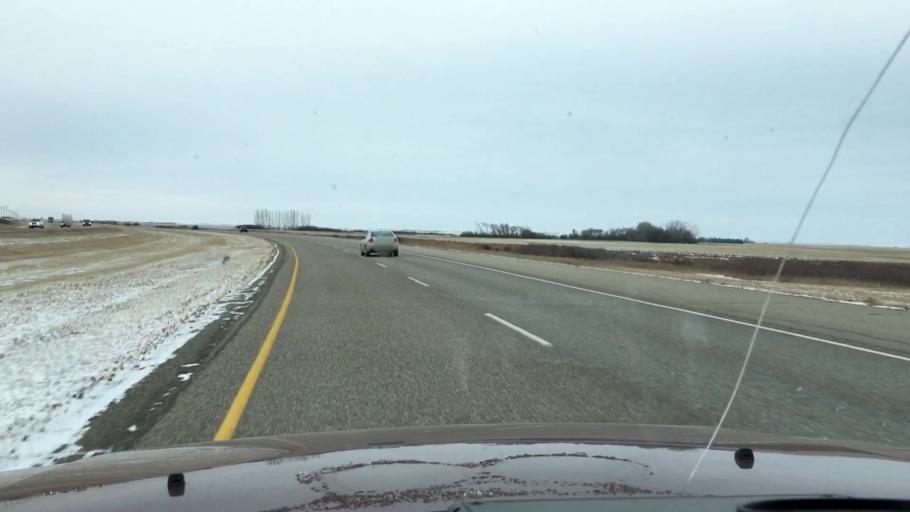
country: CA
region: Saskatchewan
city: Watrous
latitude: 51.1453
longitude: -105.9066
